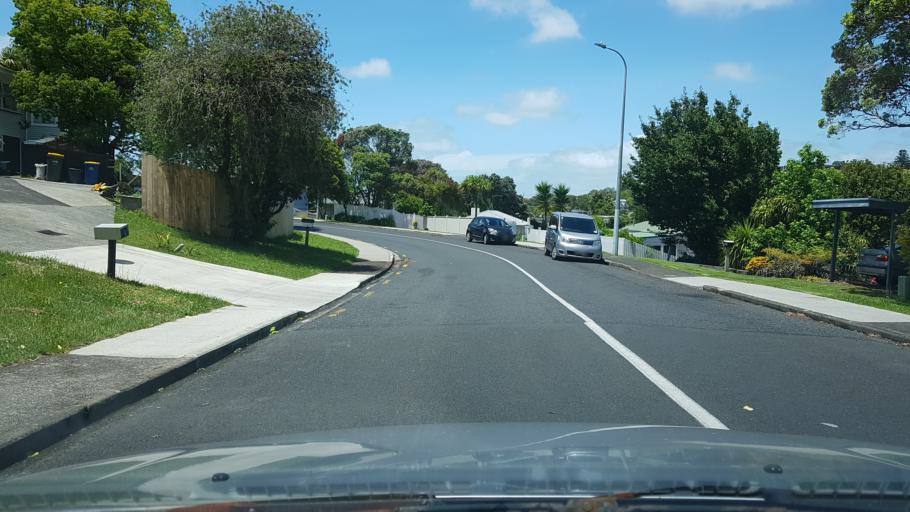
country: NZ
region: Auckland
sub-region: Auckland
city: North Shore
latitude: -36.7975
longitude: 174.7296
